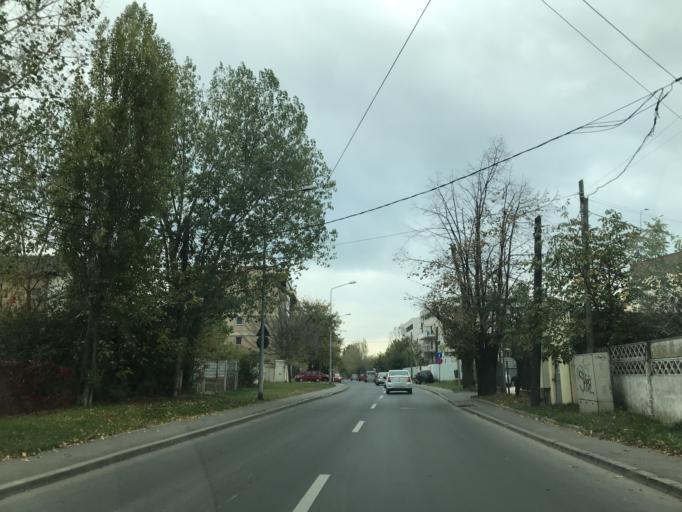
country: RO
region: Ilfov
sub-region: Comuna Otopeni
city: Otopeni
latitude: 44.4906
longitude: 26.0646
